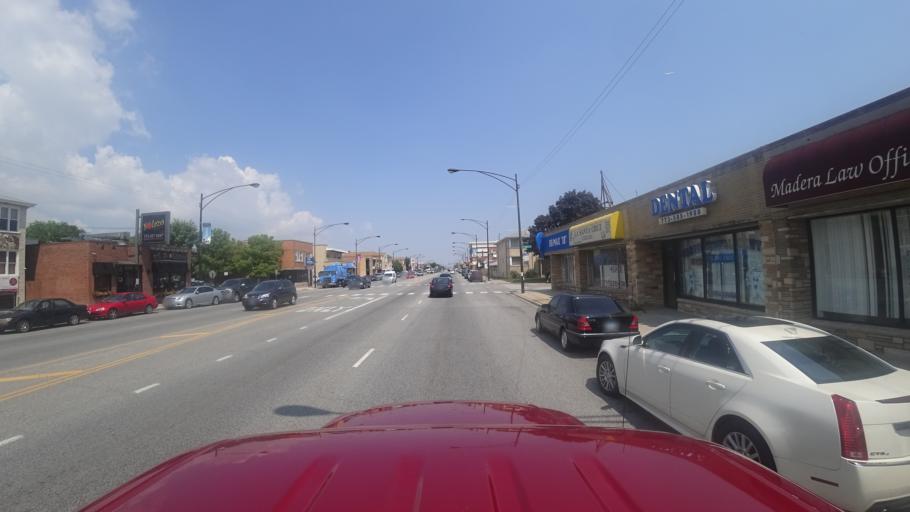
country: US
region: Illinois
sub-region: Cook County
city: Hometown
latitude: 41.7910
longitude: -87.7230
